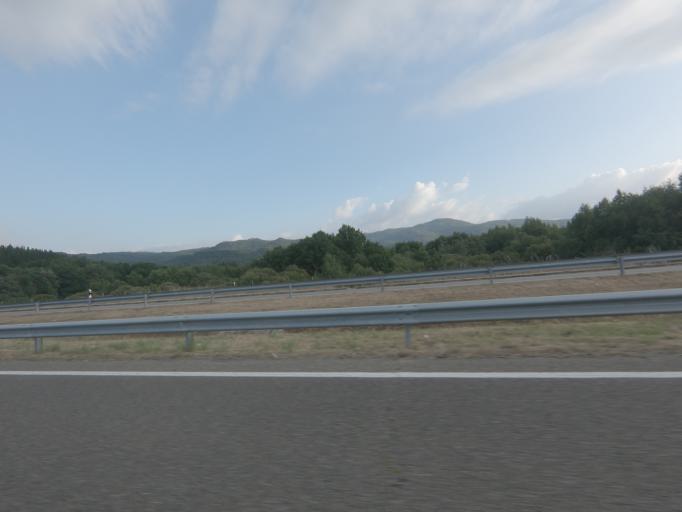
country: ES
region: Galicia
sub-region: Provincia de Ourense
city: Allariz
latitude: 42.2017
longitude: -7.7877
